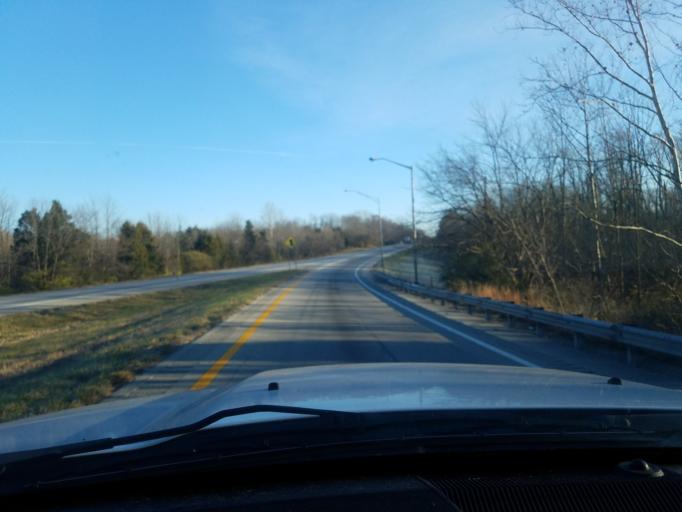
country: US
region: Kentucky
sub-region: Oldham County
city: La Grange
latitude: 38.3999
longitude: -85.3712
